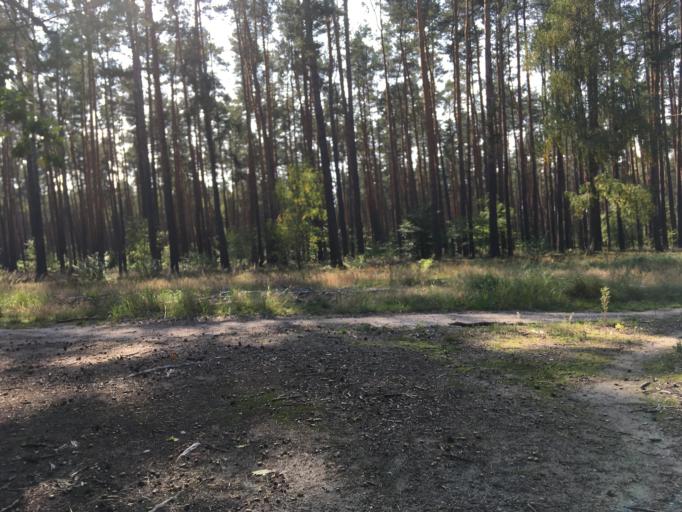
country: DE
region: Brandenburg
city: Wandlitz
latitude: 52.6936
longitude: 13.4366
